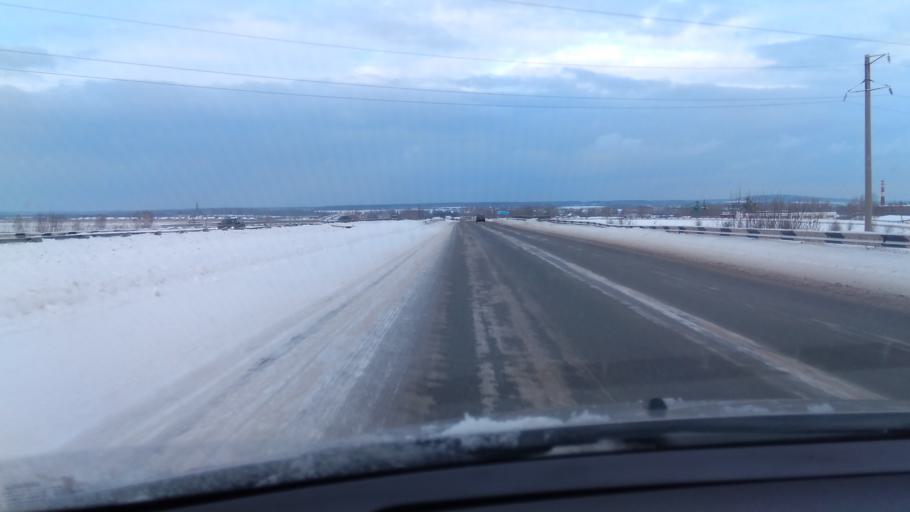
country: RU
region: Sverdlovsk
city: Tsementnyy
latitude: 57.4800
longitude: 60.1803
